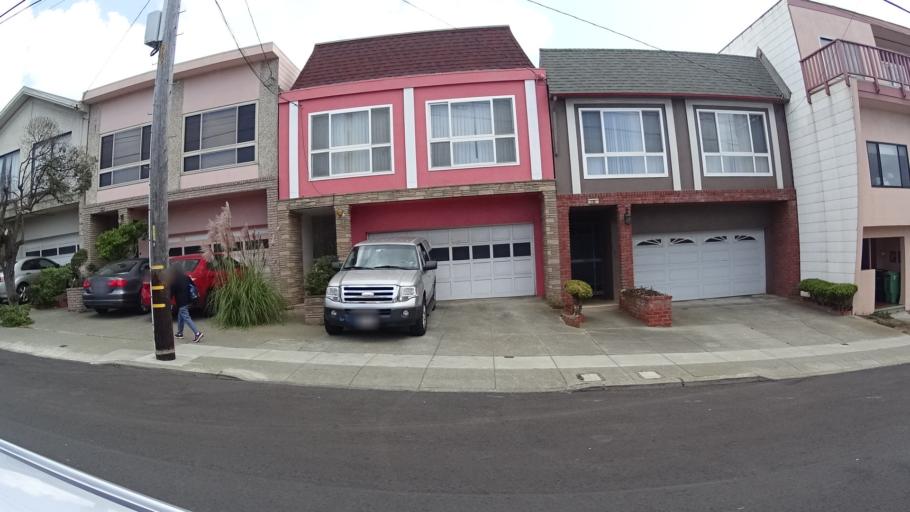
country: US
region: California
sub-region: San Mateo County
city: Daly City
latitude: 37.7425
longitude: -122.5004
